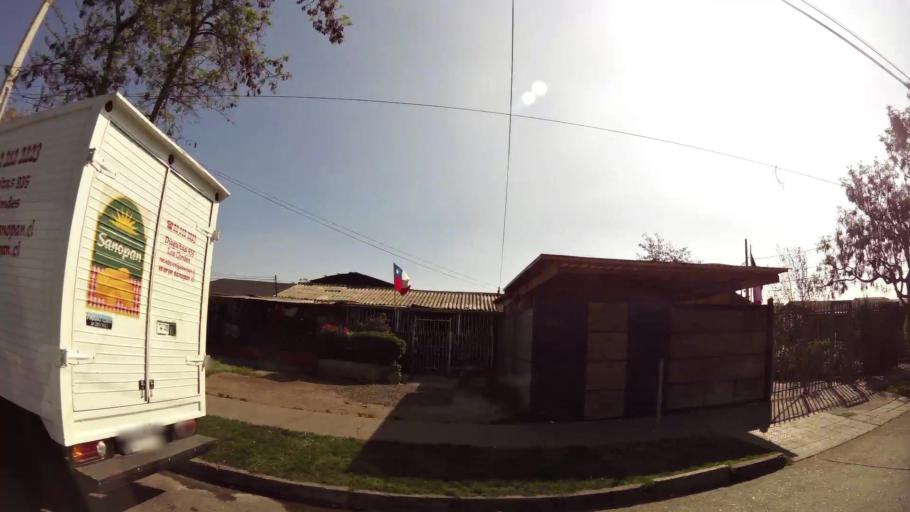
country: CL
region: Santiago Metropolitan
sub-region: Provincia de Santiago
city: Santiago
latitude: -33.4693
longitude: -70.6170
